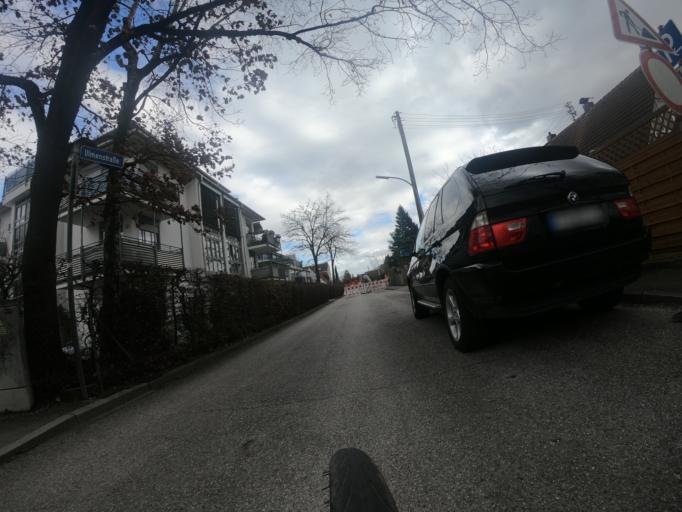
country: DE
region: Bavaria
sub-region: Upper Bavaria
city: Schongeising
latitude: 48.1601
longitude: 11.2267
